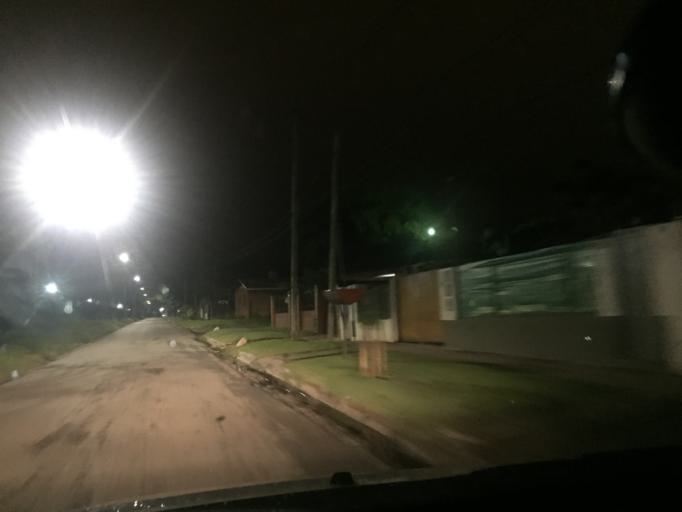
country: AR
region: Cordoba
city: Villa Allende
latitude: -31.3089
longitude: -64.2889
